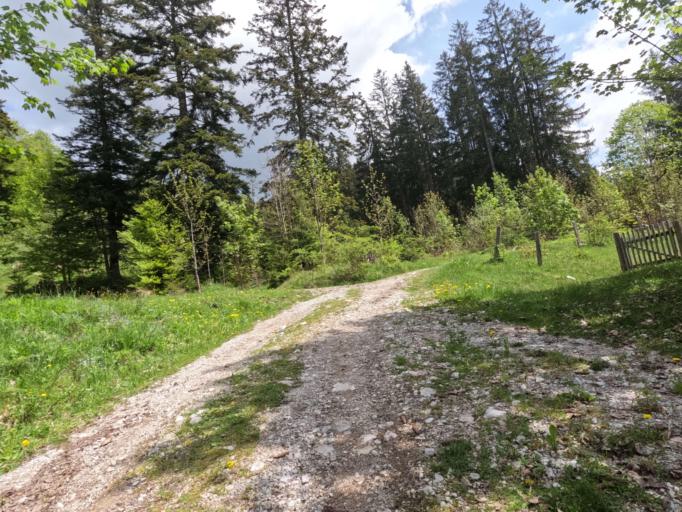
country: DE
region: Bavaria
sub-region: Upper Bavaria
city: Ruhpolding
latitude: 47.7174
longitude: 12.6962
